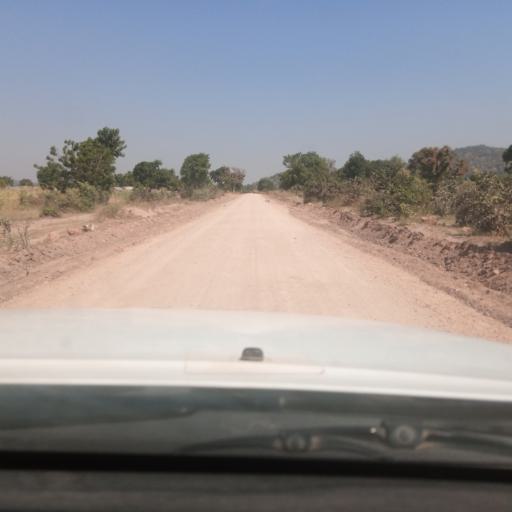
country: NG
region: Adamawa
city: Yola
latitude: 9.0602
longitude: 12.3867
